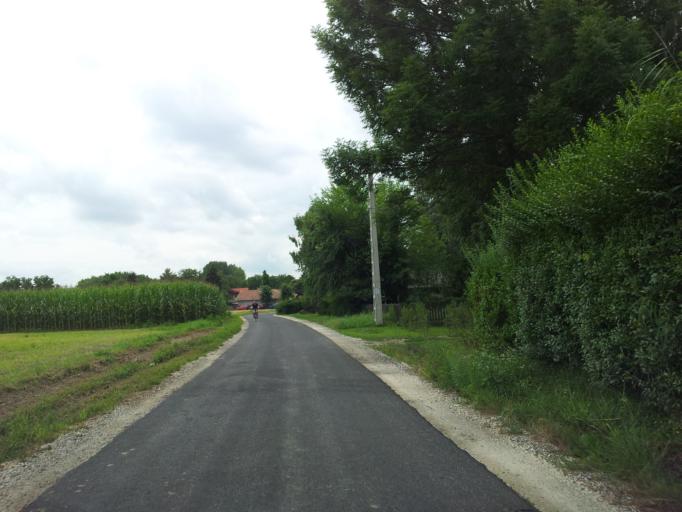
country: HU
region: Pest
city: Rackeve
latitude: 47.1766
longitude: 18.9525
